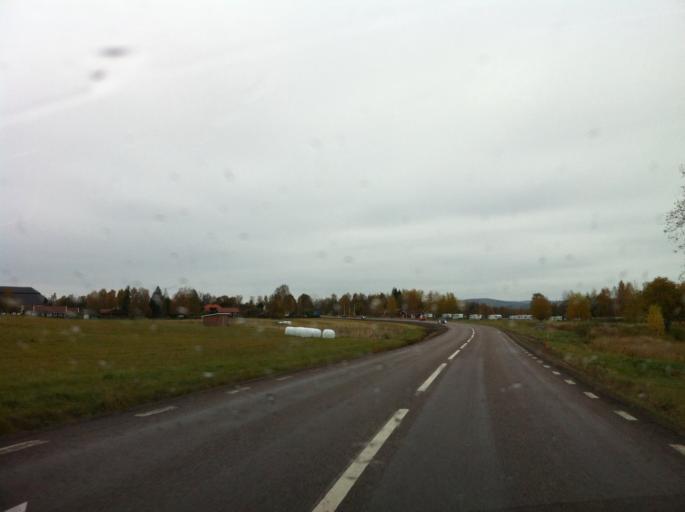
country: SE
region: Dalarna
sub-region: Ludvika Kommun
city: Grangesberg
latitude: 60.2448
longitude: 14.9800
